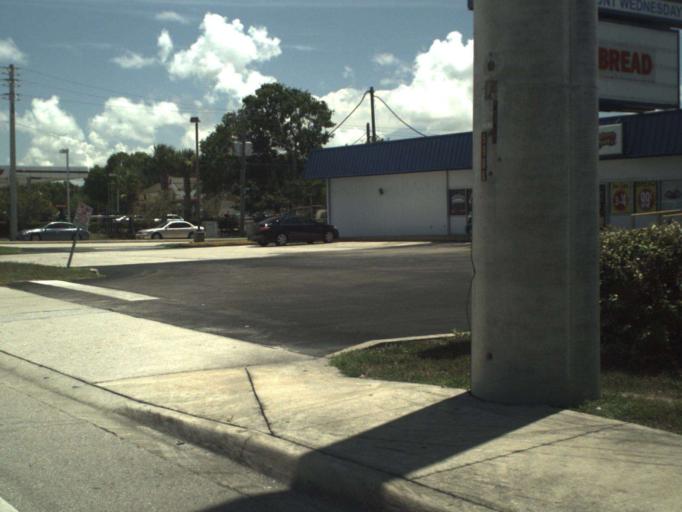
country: US
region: Florida
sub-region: Saint Lucie County
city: Indian River Estates
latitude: 27.3456
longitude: -80.3260
